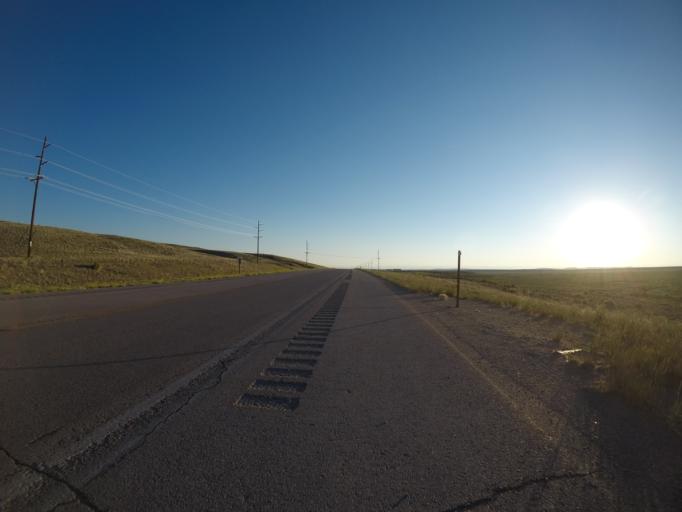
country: US
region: Wyoming
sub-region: Sublette County
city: Marbleton
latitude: 42.5717
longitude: -110.0953
